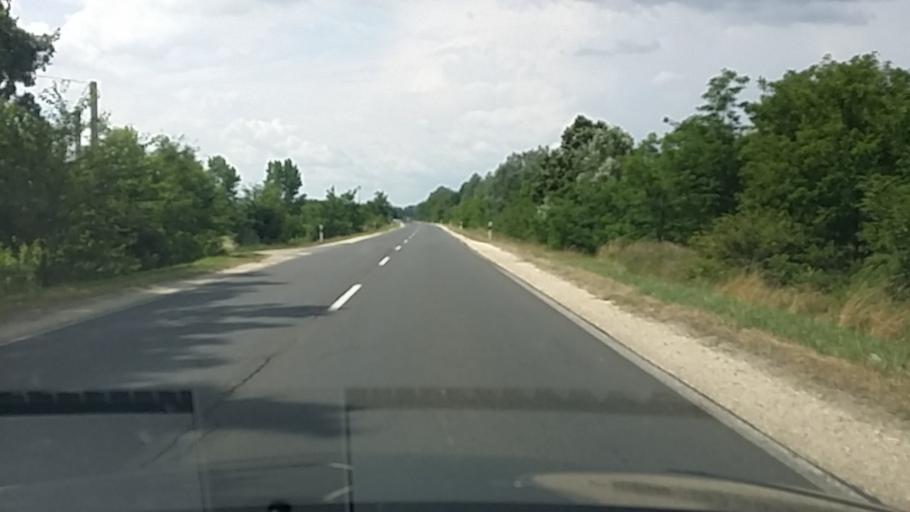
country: HU
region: Pest
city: Taborfalva
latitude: 47.0851
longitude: 19.4849
